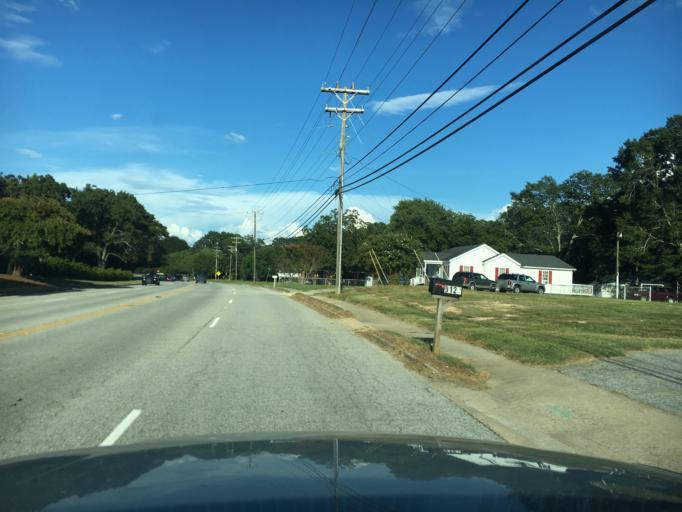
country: US
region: South Carolina
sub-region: Greenville County
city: Simpsonville
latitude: 34.7403
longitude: -82.2372
